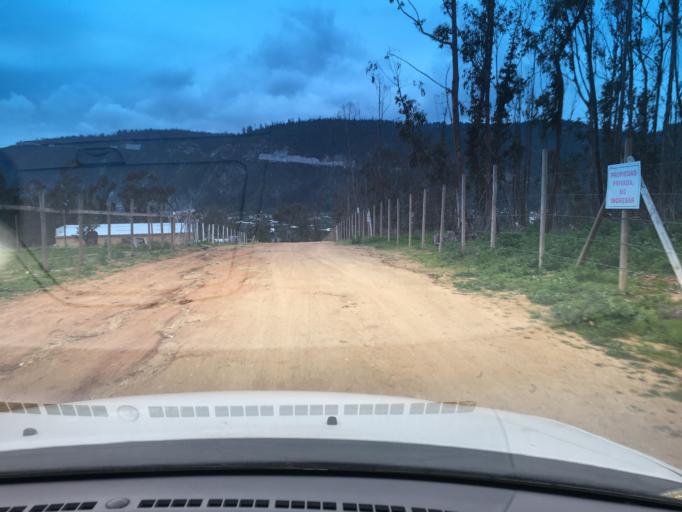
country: CL
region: Valparaiso
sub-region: Provincia de Valparaiso
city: Valparaiso
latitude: -33.1060
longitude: -71.6718
